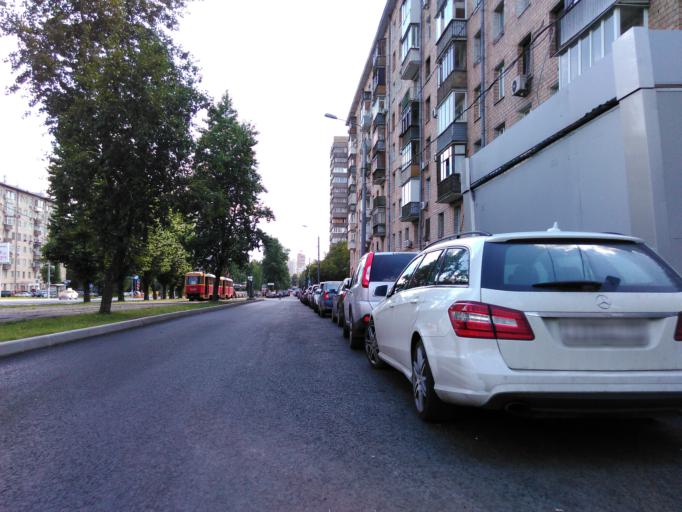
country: RU
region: Moskovskaya
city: Semenovskoye
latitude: 55.6871
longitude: 37.5462
